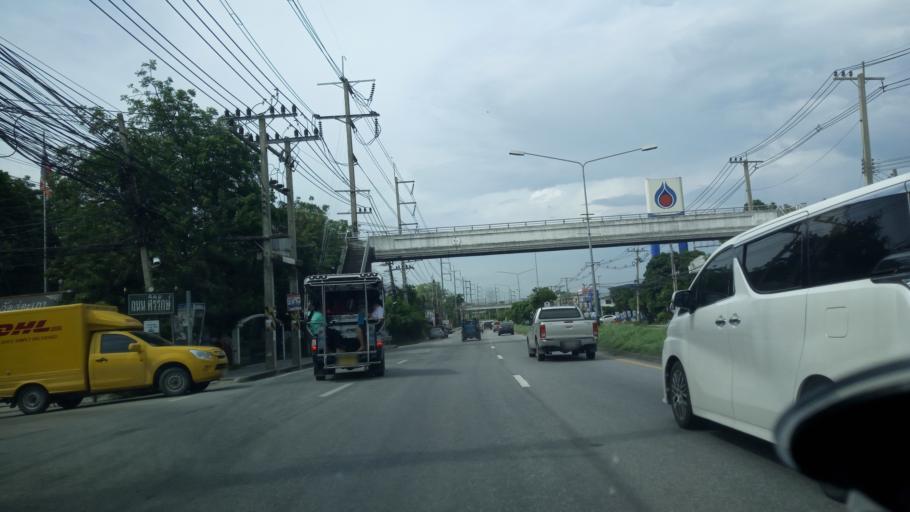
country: TH
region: Chon Buri
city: Chon Buri
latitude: 13.3951
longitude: 101.0231
